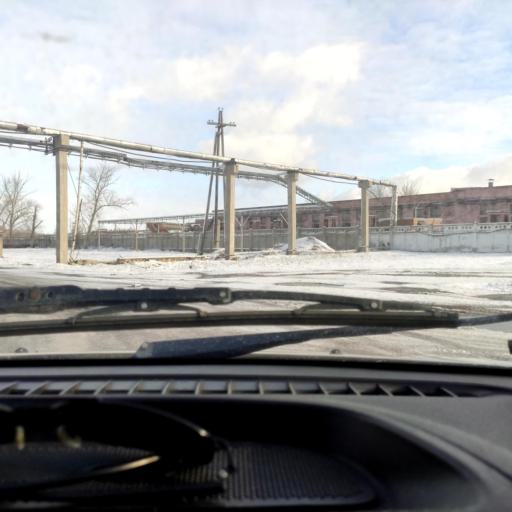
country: RU
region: Samara
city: Zhigulevsk
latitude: 53.5342
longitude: 49.4815
